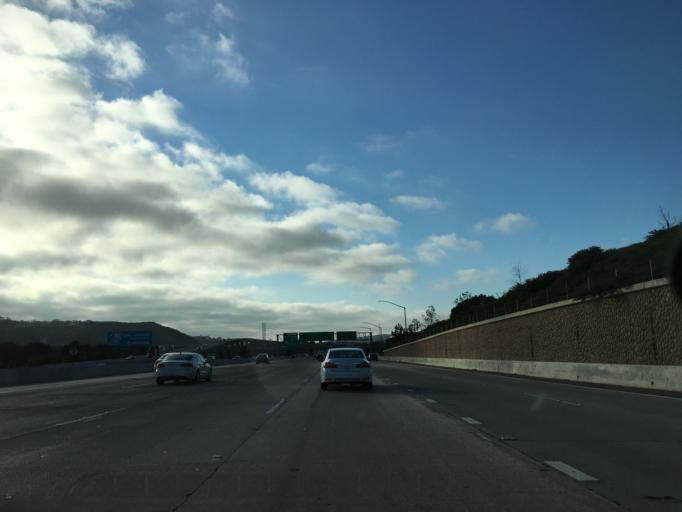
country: US
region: California
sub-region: San Diego County
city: Del Mar
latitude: 32.8995
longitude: -117.2190
